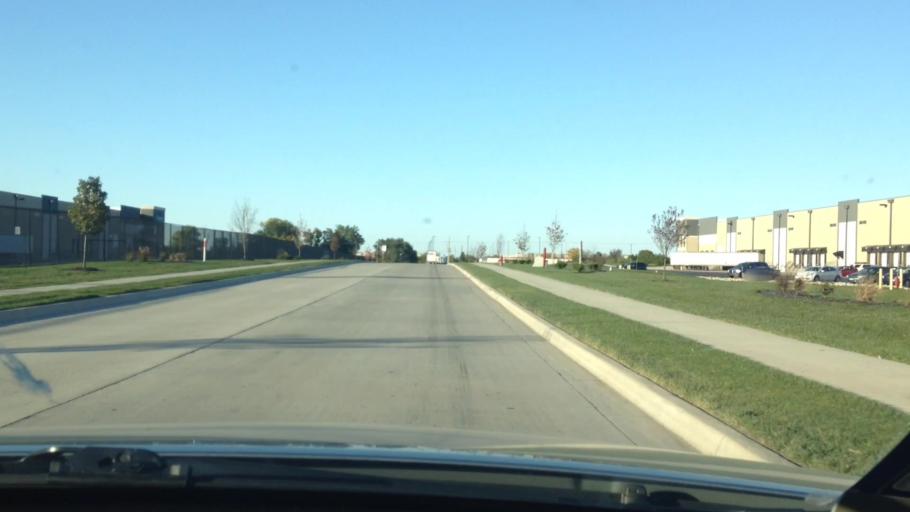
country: US
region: Kansas
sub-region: Johnson County
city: Gardner
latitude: 38.7788
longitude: -94.9423
